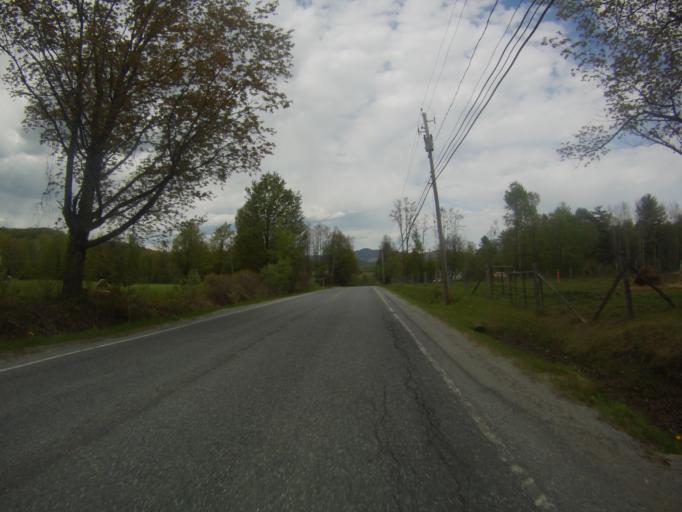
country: US
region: New York
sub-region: Essex County
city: Port Henry
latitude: 44.0141
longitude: -73.5001
